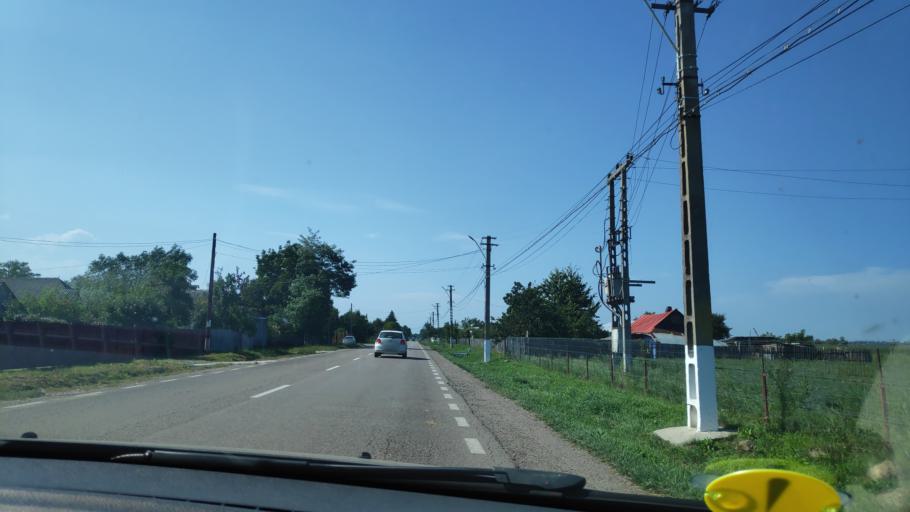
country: RO
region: Suceava
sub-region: Comuna Boroaia
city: Boroaia
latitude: 47.3593
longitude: 26.3428
